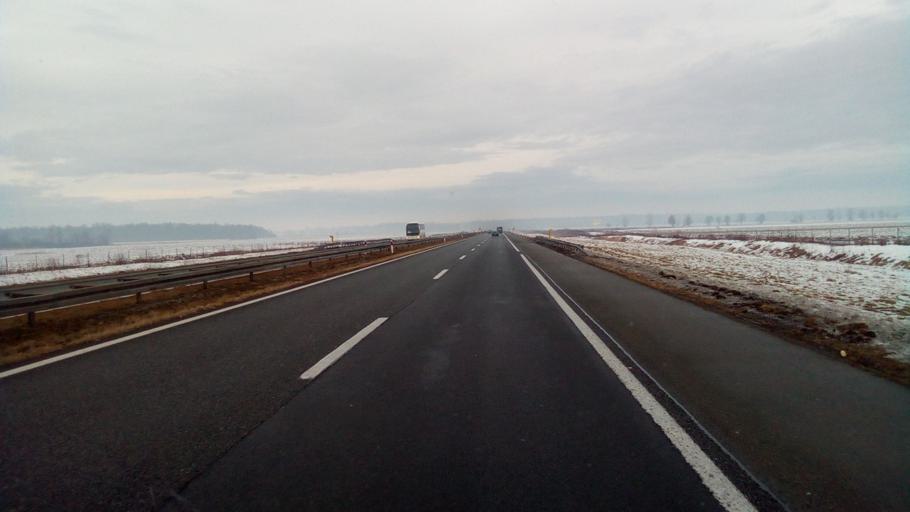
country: HR
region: Zagrebacka
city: Lupoglav
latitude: 45.7219
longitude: 16.3446
